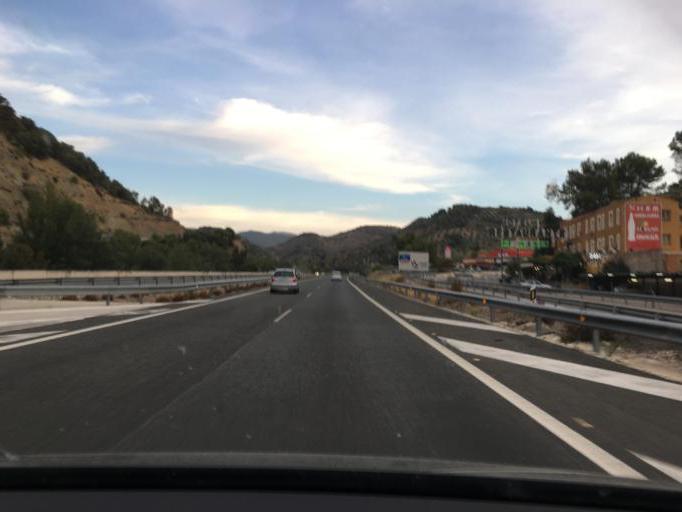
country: ES
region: Andalusia
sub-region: Provincia de Jaen
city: Cambil
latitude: 37.6807
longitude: -3.6268
